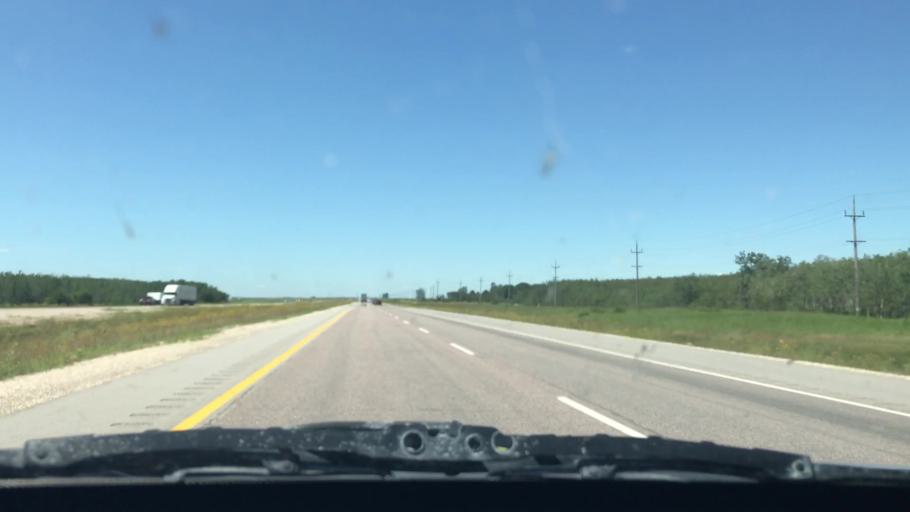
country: CA
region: Manitoba
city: Steinbach
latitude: 49.6853
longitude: -96.6062
